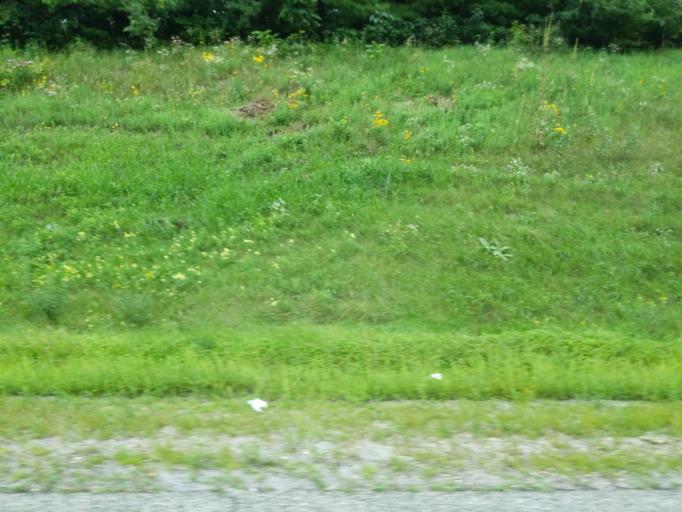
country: US
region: Wisconsin
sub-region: Sauk County
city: Sauk City
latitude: 43.2503
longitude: -89.7211
